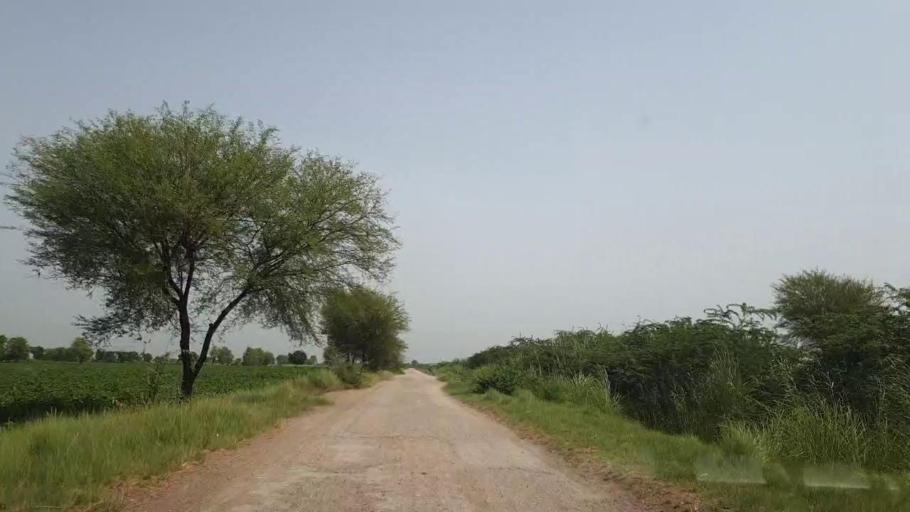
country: PK
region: Sindh
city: Sakrand
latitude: 26.1359
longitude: 68.3642
